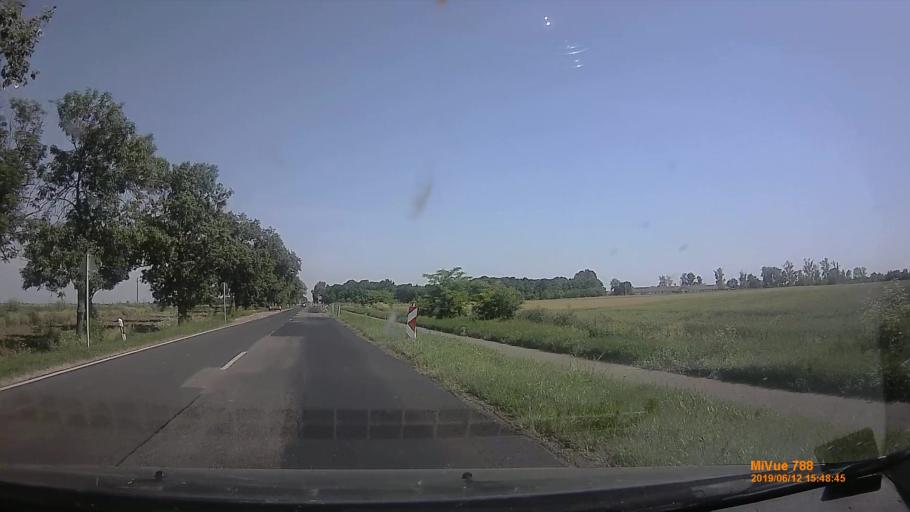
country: HU
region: Csongrad
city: Apatfalva
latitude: 46.1998
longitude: 20.5533
